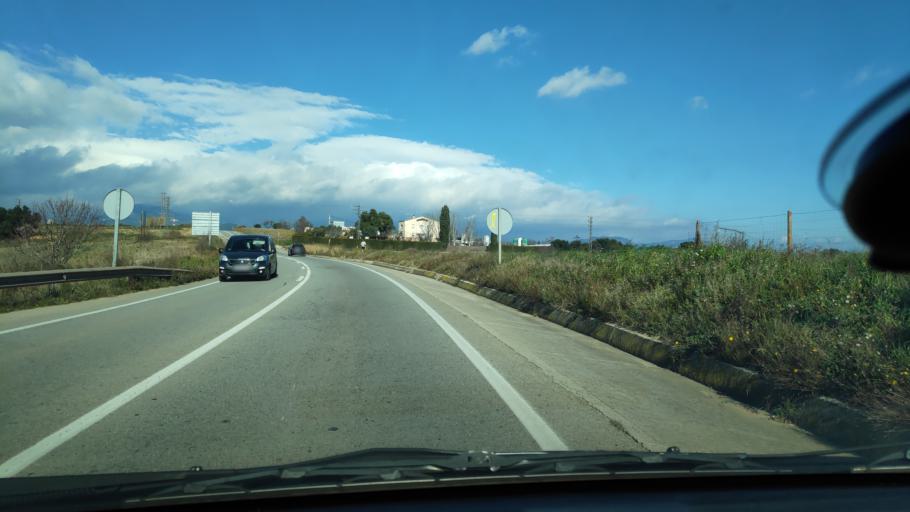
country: ES
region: Catalonia
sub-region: Provincia de Barcelona
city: Sant Quirze del Valles
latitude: 41.5465
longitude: 2.0688
